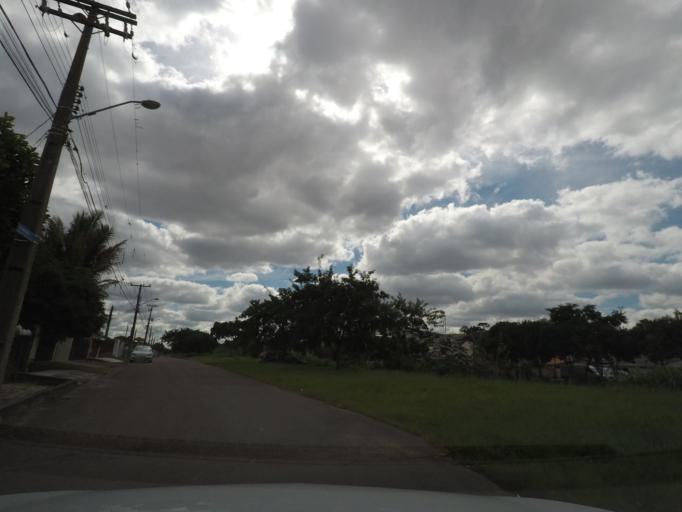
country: BR
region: Parana
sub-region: Sao Jose Dos Pinhais
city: Sao Jose dos Pinhais
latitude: -25.4882
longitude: -49.2329
